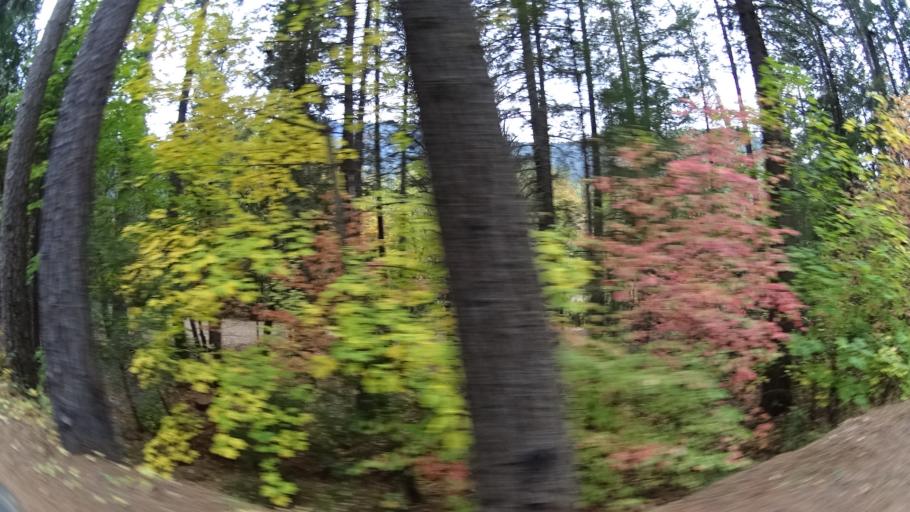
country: US
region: California
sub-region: Siskiyou County
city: Happy Camp
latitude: 41.8634
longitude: -123.4023
